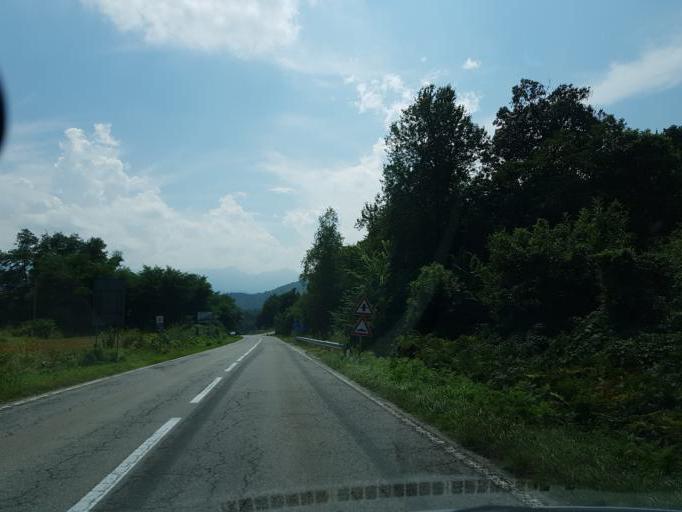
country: IT
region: Piedmont
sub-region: Provincia di Cuneo
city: Vignolo
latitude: 44.3519
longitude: 7.4772
